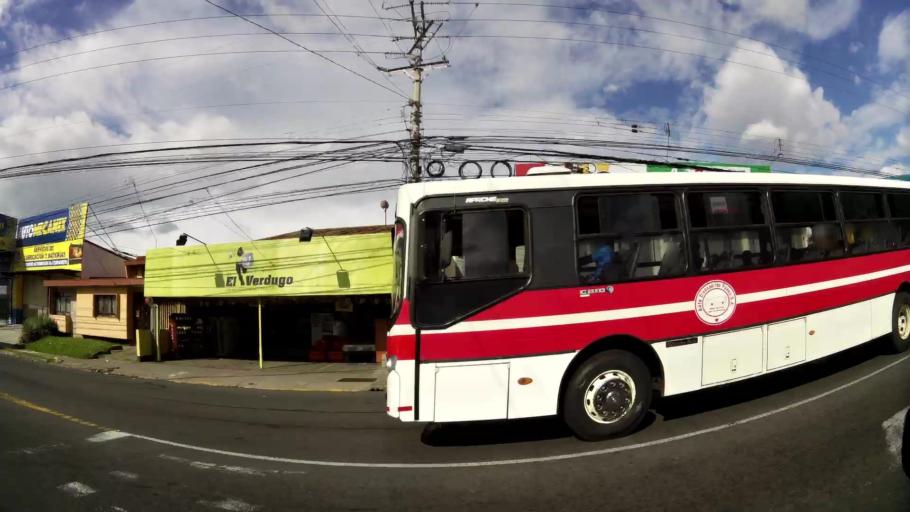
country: CR
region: San Jose
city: San Rafael
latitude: 9.9413
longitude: -84.1223
